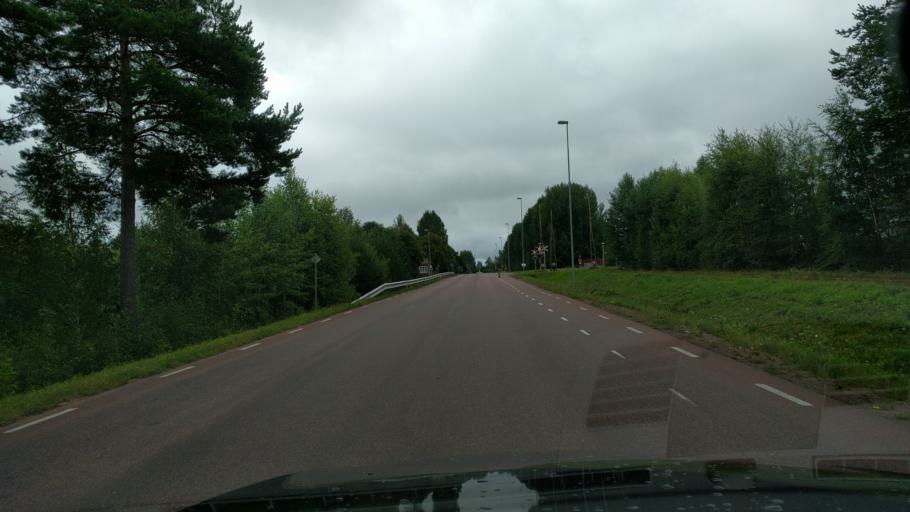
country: SE
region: Dalarna
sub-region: Mora Kommun
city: Mora
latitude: 61.0059
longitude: 14.5215
